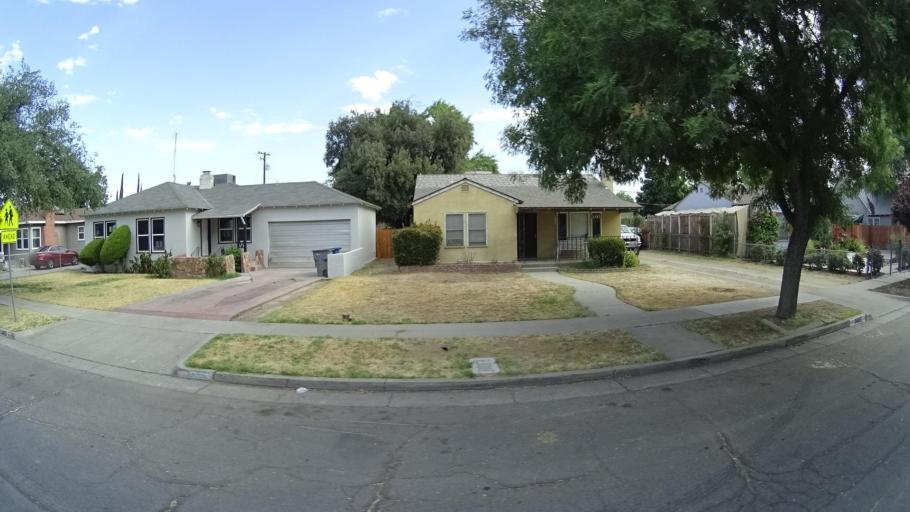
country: US
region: California
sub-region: Fresno County
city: Fresno
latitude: 36.7623
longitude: -119.7668
